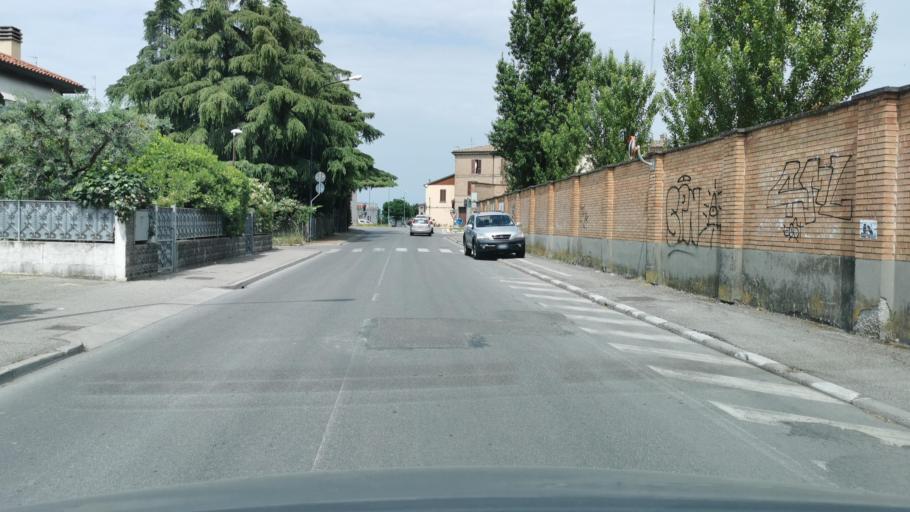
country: IT
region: Emilia-Romagna
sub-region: Provincia di Ravenna
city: Bagnacavallo
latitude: 44.4182
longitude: 11.9734
